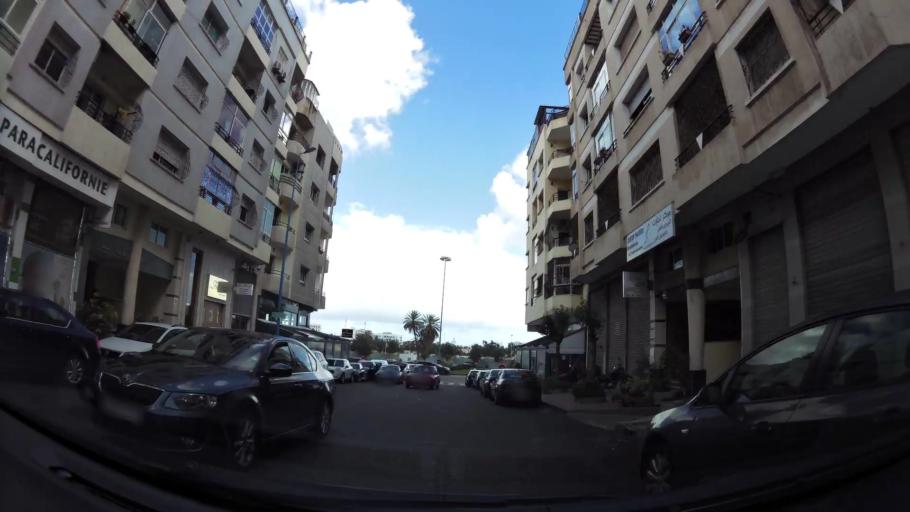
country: MA
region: Grand Casablanca
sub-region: Casablanca
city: Casablanca
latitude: 33.5557
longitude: -7.6270
